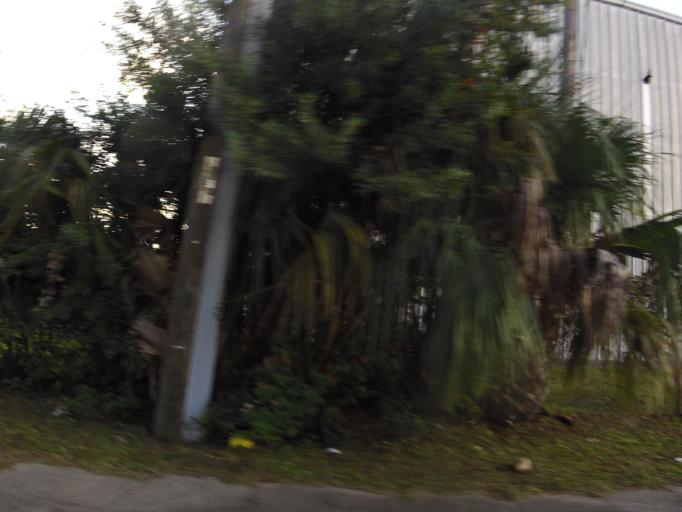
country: US
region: Florida
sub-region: Duval County
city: Jacksonville
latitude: 30.3369
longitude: -81.6910
